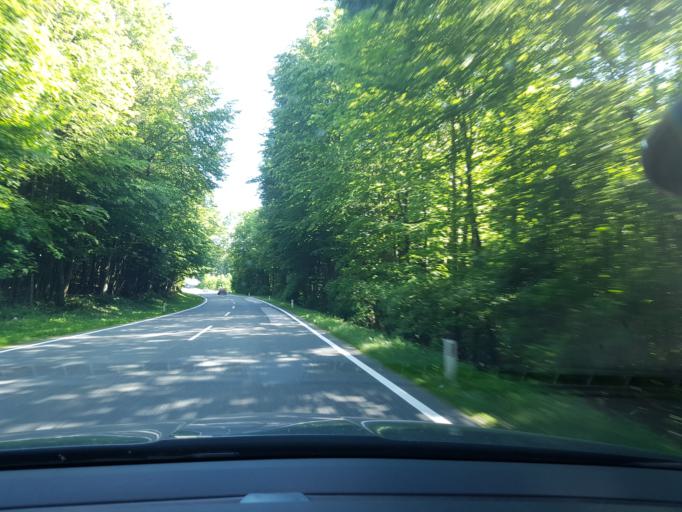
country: AT
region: Salzburg
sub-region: Politischer Bezirk Salzburg-Umgebung
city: Obertrum am See
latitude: 47.9160
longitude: 13.0829
